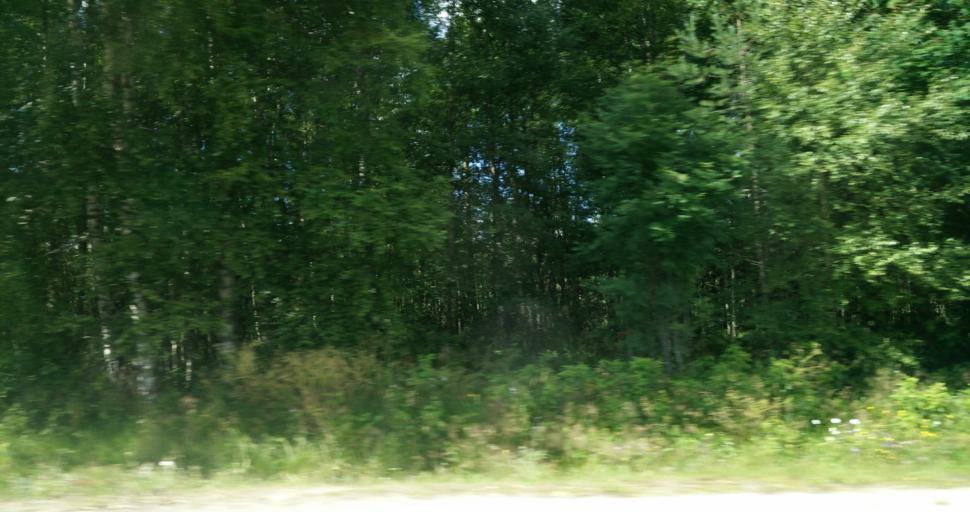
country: SE
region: Vaermland
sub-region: Hagfors Kommun
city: Ekshaerad
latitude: 60.0428
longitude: 13.4935
